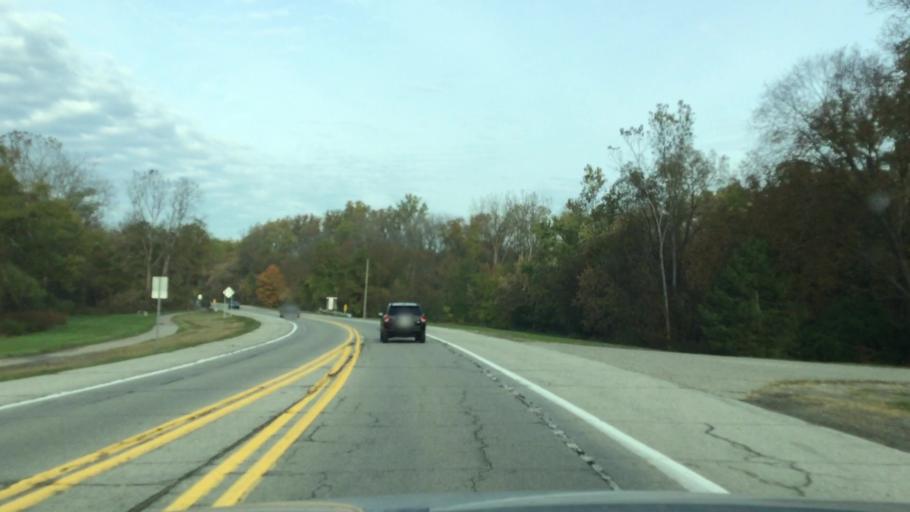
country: US
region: Michigan
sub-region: Wayne County
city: Dearborn Heights
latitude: 42.3299
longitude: -83.2461
